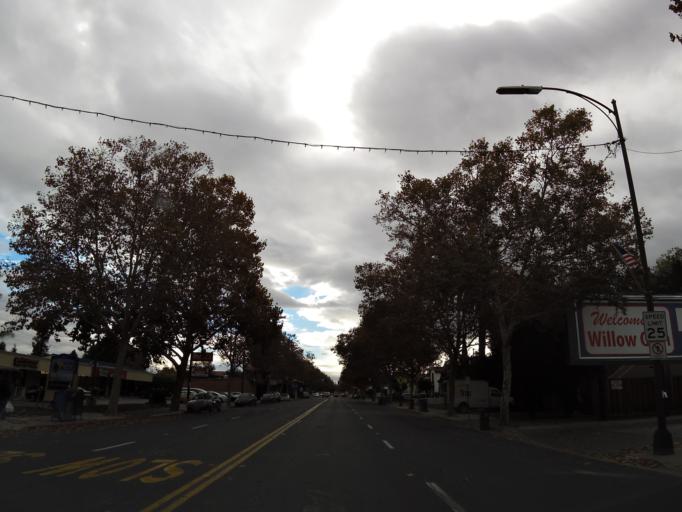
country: US
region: California
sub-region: Santa Clara County
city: Buena Vista
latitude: 37.3103
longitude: -121.9024
